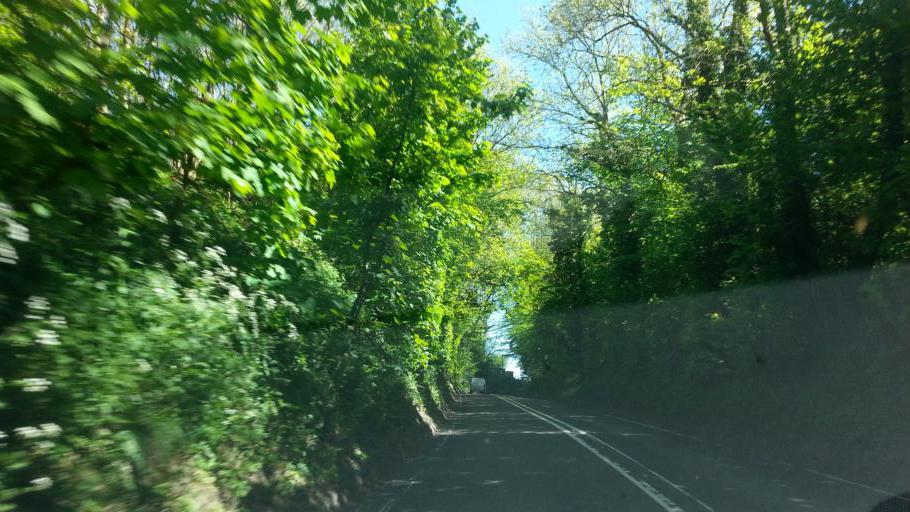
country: GB
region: England
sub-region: Dorset
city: Shaftesbury
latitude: 51.0263
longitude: -2.1897
